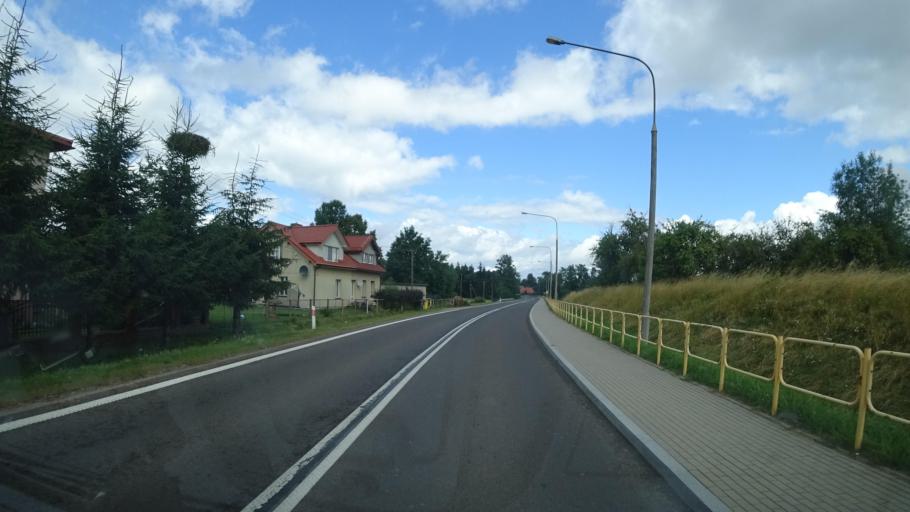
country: PL
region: Warmian-Masurian Voivodeship
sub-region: Powiat olecki
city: Kowale Oleckie
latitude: 54.2058
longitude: 22.4114
